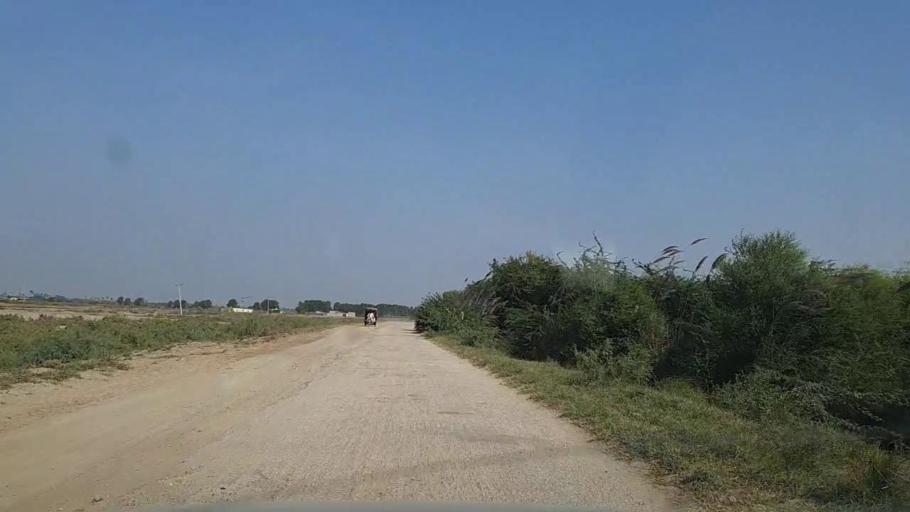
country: PK
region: Sindh
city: Mirpur Sakro
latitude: 24.5611
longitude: 67.6089
